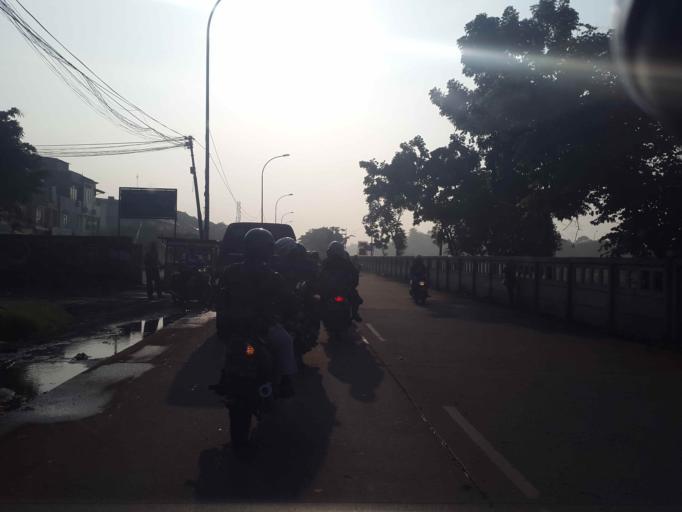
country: ID
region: West Java
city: Bekasi
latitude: -6.2734
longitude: 107.0522
